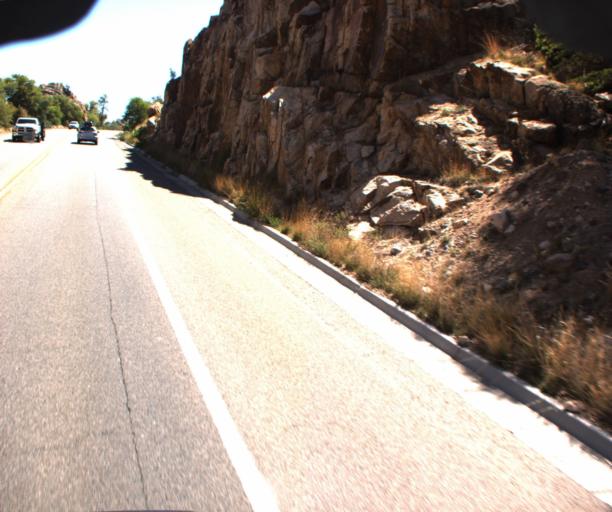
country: US
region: Arizona
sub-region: Yavapai County
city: Prescott
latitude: 34.6048
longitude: -112.4228
